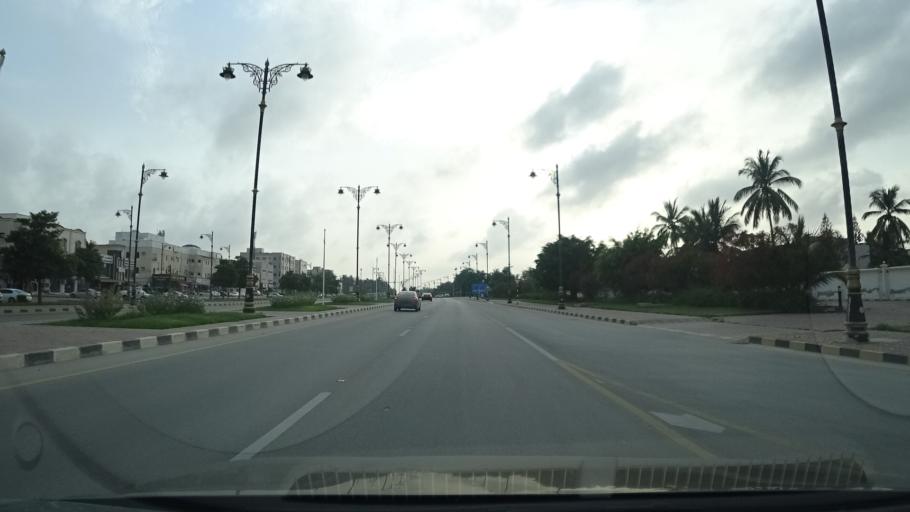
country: OM
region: Zufar
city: Salalah
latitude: 17.0262
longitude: 54.1602
